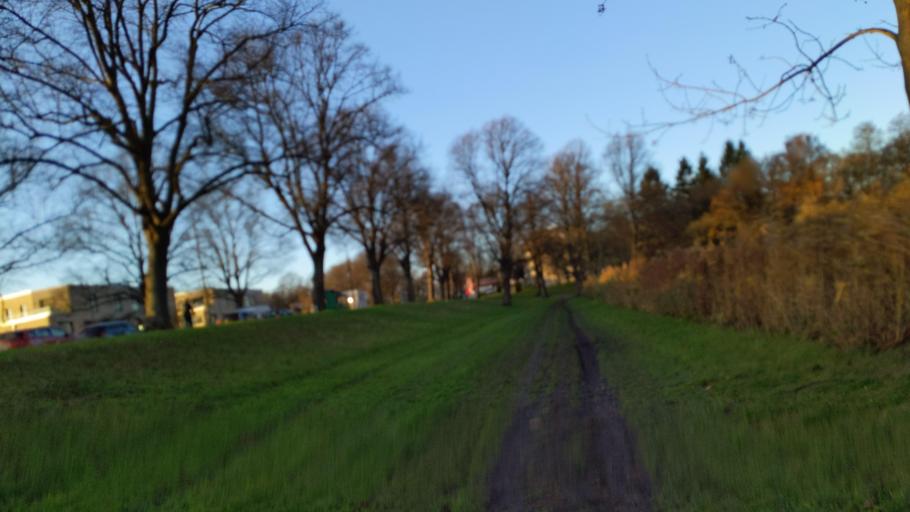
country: DE
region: Schleswig-Holstein
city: Luebeck
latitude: 53.8731
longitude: 10.6970
